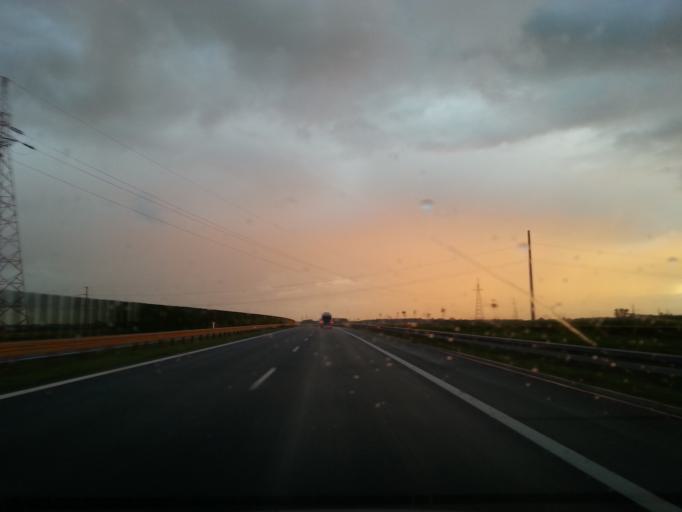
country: PL
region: Lower Silesian Voivodeship
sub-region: Powiat wroclawski
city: Mirkow
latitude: 51.2133
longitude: 17.1327
